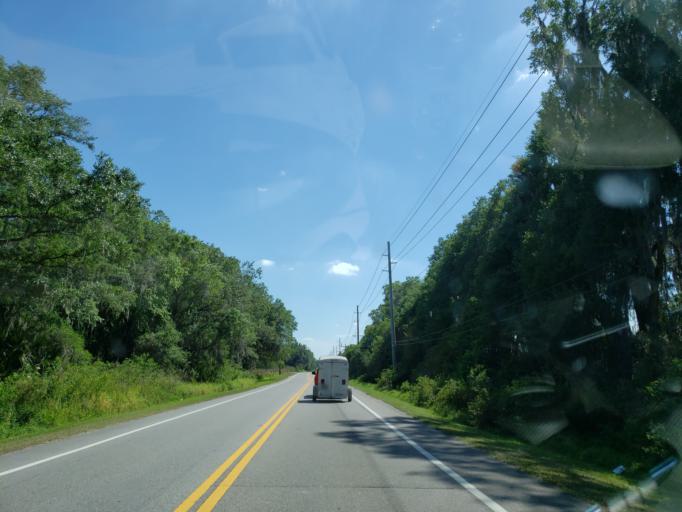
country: US
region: Florida
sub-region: Hillsborough County
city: Plant City
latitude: 27.9172
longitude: -82.1263
